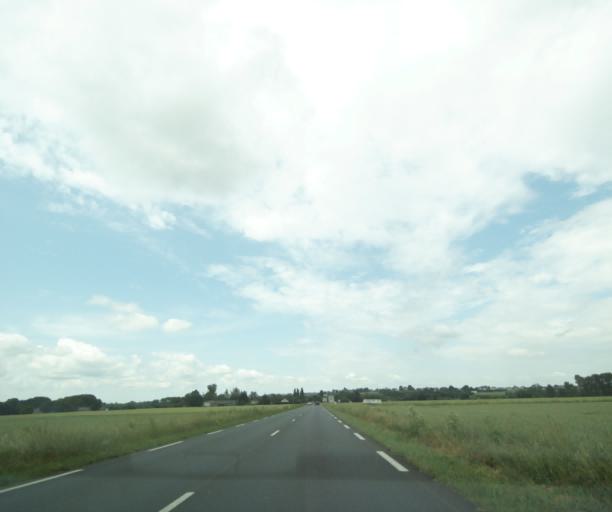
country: FR
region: Pays de la Loire
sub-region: Departement de Maine-et-Loire
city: Montreuil-Bellay
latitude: 47.1162
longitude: -0.1619
